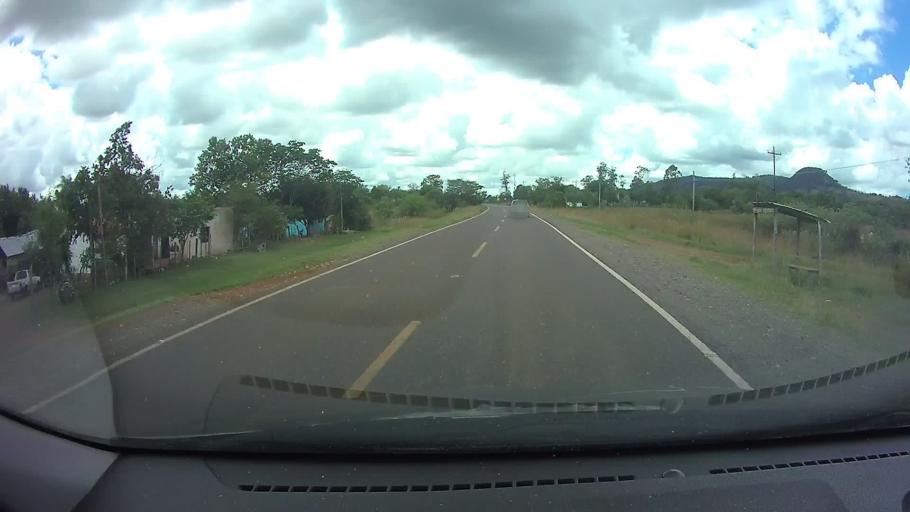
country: PY
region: Paraguari
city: Ybycui
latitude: -25.9101
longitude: -56.9885
